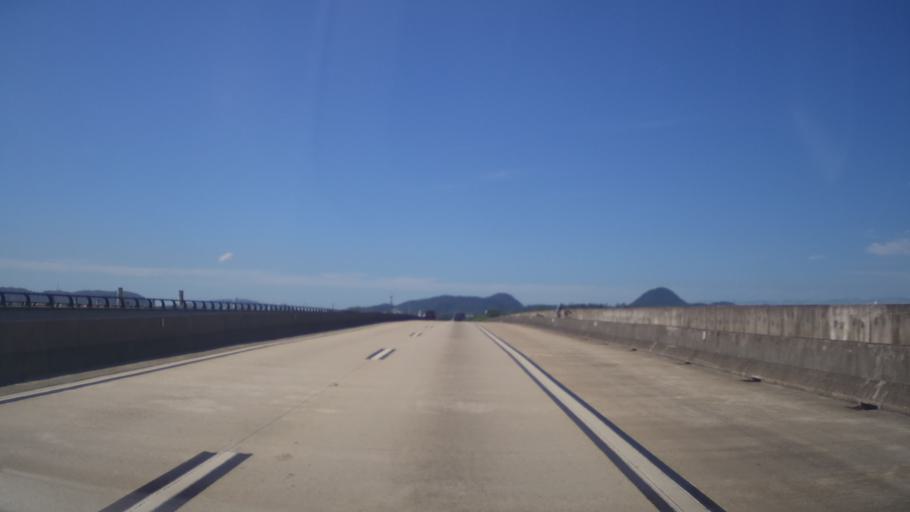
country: BR
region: Sao Paulo
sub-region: Cubatao
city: Cubatao
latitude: -23.9353
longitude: -46.4255
